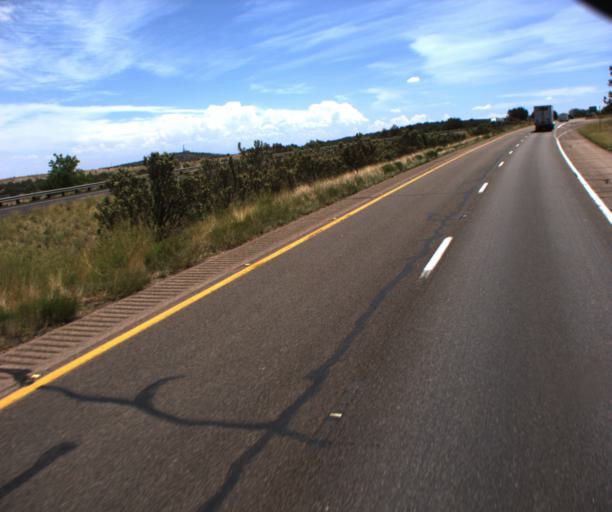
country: US
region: Arizona
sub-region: Yavapai County
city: Paulden
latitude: 35.2718
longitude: -112.7356
